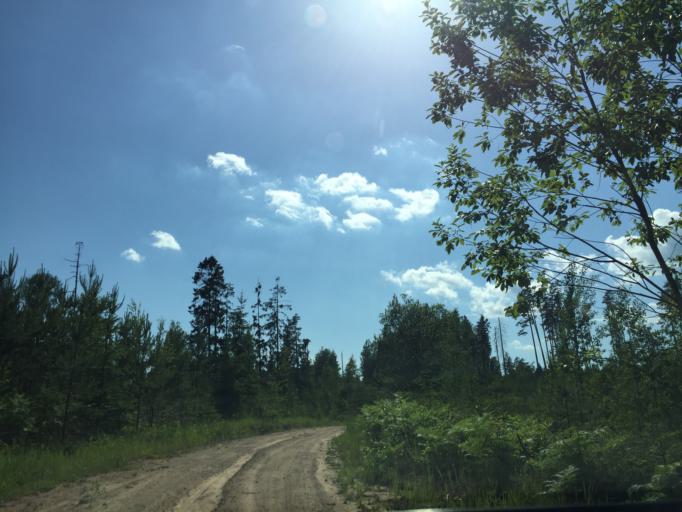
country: LV
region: Tukuma Rajons
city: Tukums
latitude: 57.0198
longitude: 23.2314
